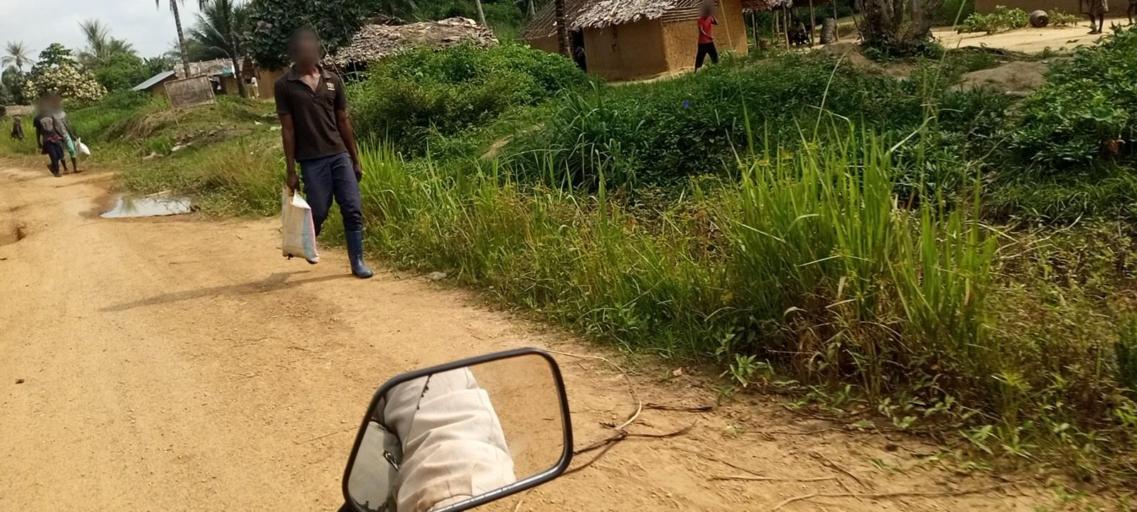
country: CD
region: Eastern Province
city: Kisangani
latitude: 0.4028
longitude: 25.3828
